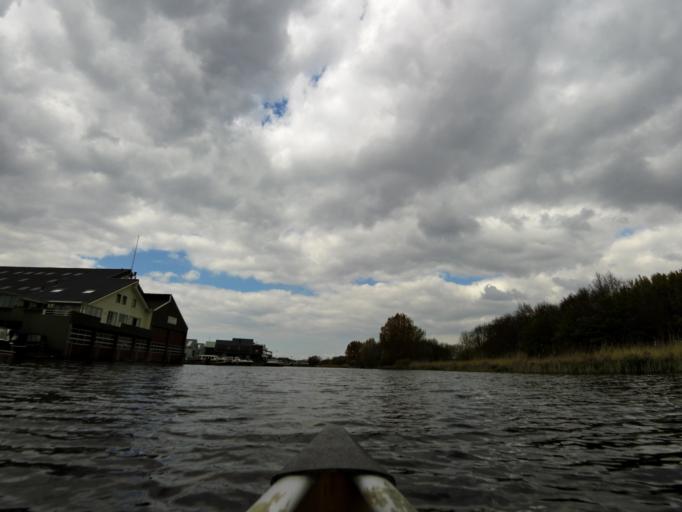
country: NL
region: South Holland
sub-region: Gemeente Leiden
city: Leiden
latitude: 52.1893
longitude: 4.5052
